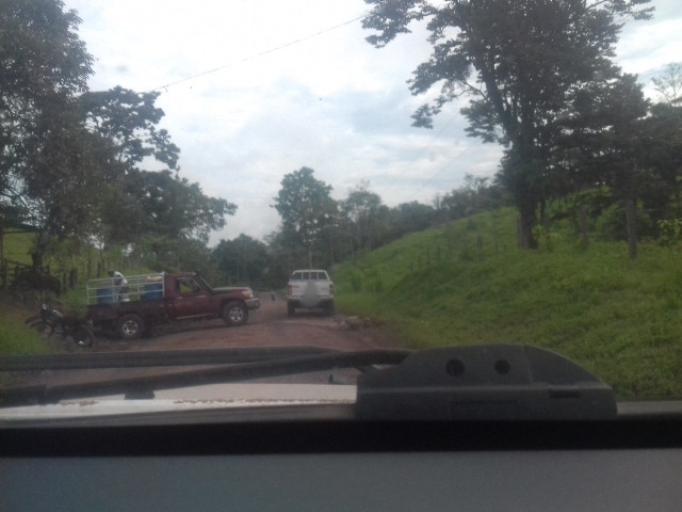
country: NI
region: Atlantico Norte (RAAN)
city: Waslala
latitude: 13.4211
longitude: -85.3161
